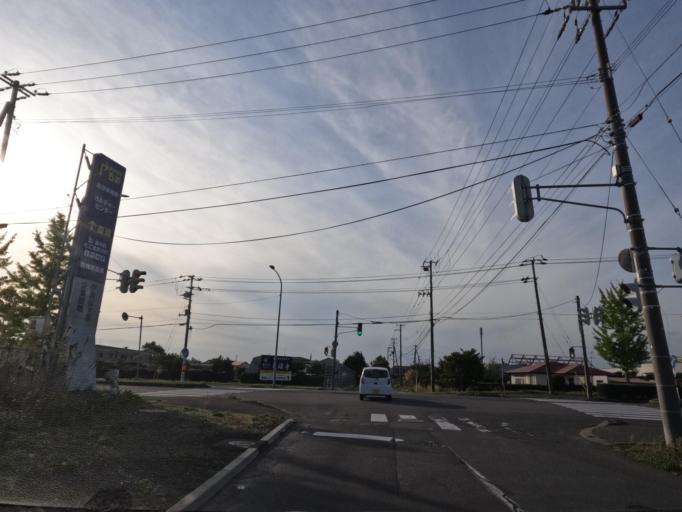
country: JP
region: Hokkaido
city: Date
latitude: 42.4756
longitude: 140.8848
